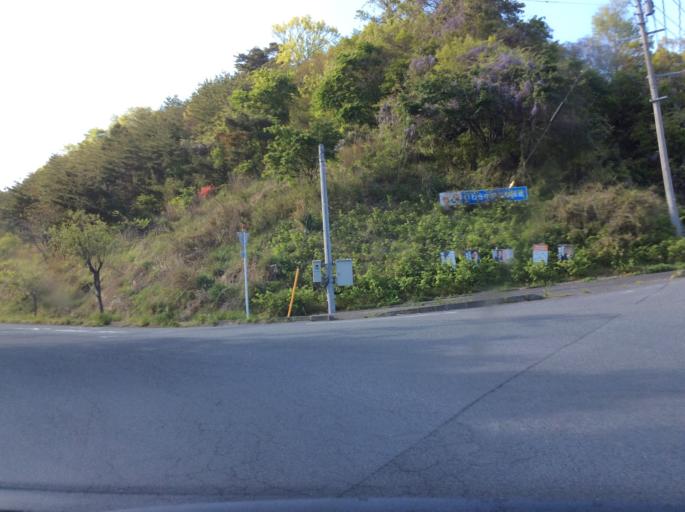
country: JP
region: Fukushima
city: Iwaki
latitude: 36.9636
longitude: 140.8492
